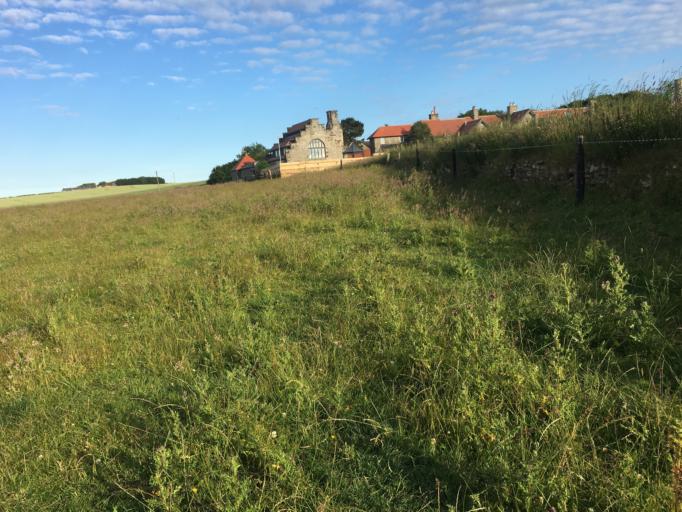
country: GB
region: England
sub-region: Northumberland
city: Bamburgh
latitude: 55.6031
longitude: -1.7019
